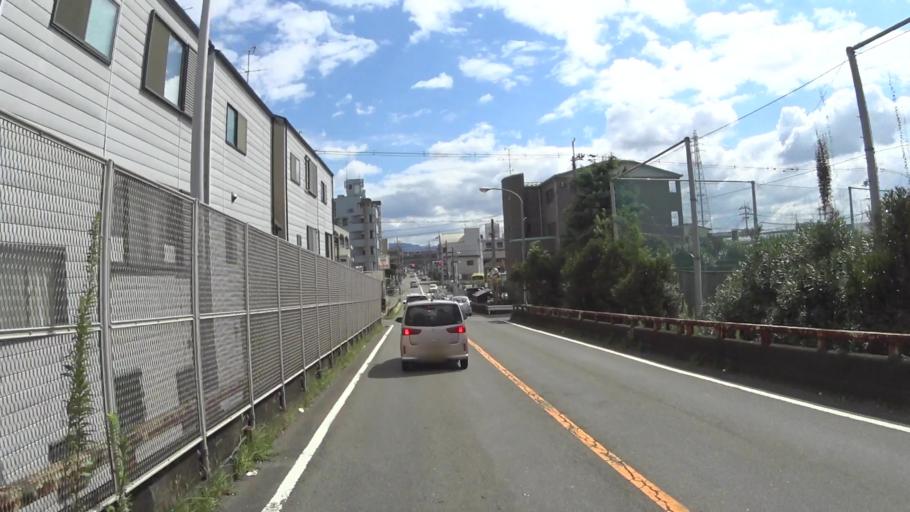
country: JP
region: Kyoto
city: Muko
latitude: 34.9597
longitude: 135.7108
